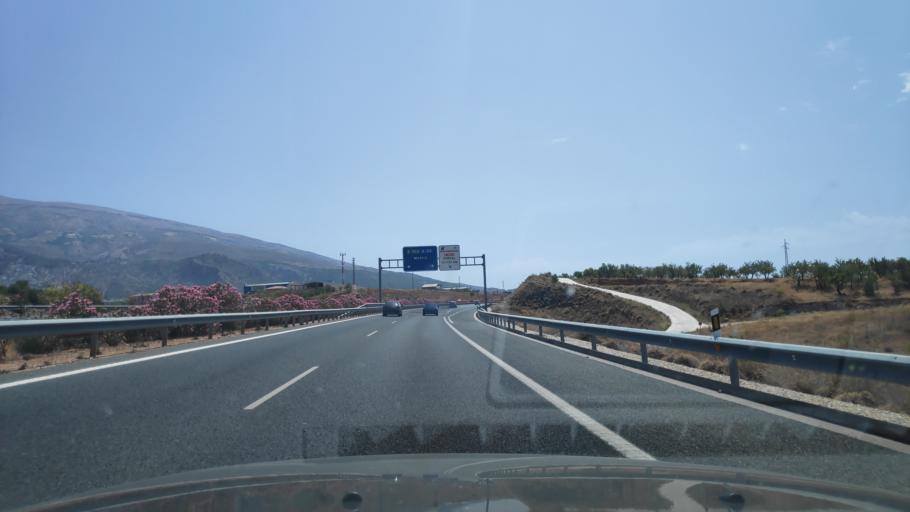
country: ES
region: Andalusia
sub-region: Provincia de Granada
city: Durcal
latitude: 36.9786
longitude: -3.5658
